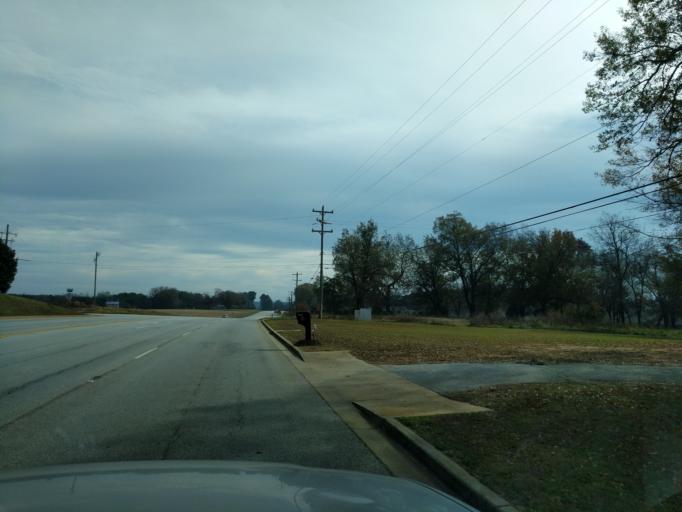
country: US
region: South Carolina
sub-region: Spartanburg County
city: Roebuck
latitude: 34.8776
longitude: -82.0461
